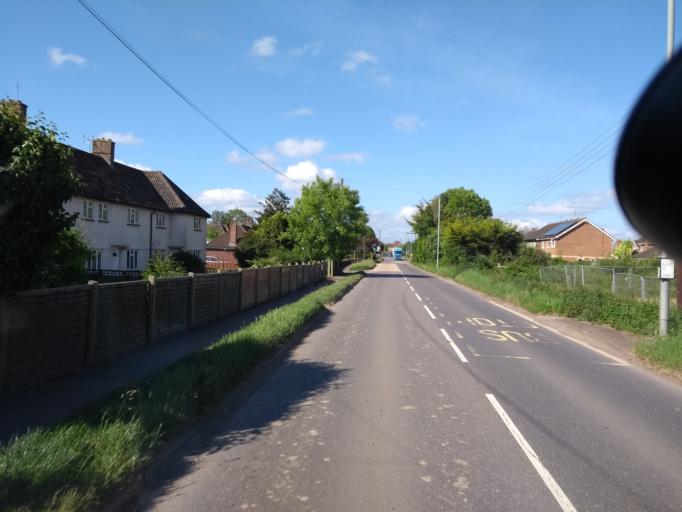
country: GB
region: England
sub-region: Somerset
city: Creech Saint Michael
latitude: 51.0380
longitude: -3.0611
